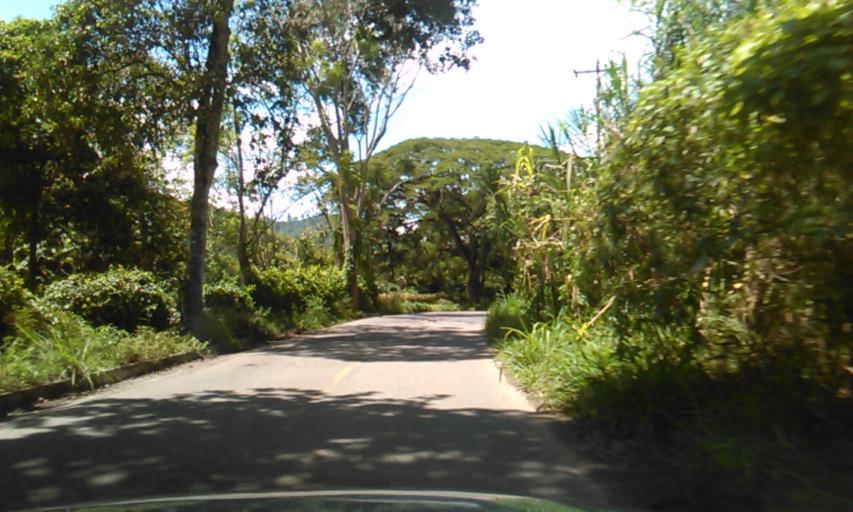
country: CO
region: Quindio
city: Cordoba
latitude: 4.4056
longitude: -75.7059
